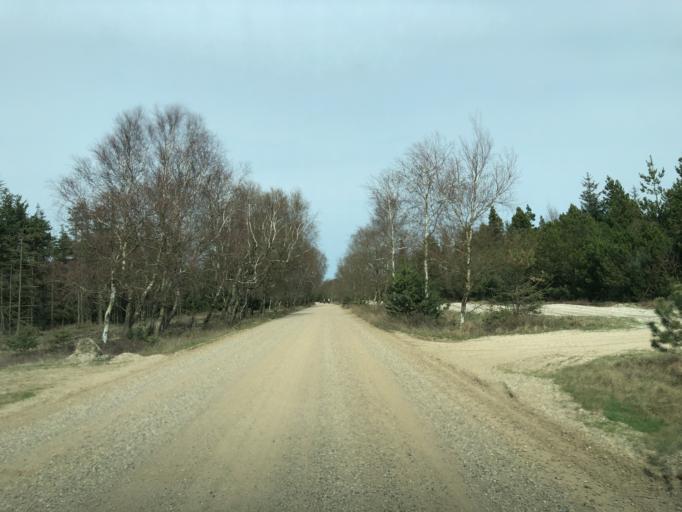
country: DK
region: South Denmark
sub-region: Varde Kommune
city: Oksbol
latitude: 55.6114
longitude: 8.1644
